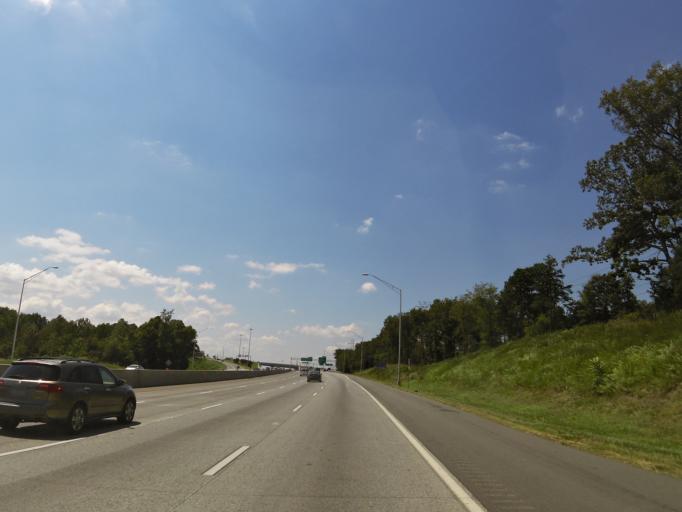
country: US
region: North Carolina
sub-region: Cabarrus County
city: Kannapolis
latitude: 35.4381
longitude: -80.6511
